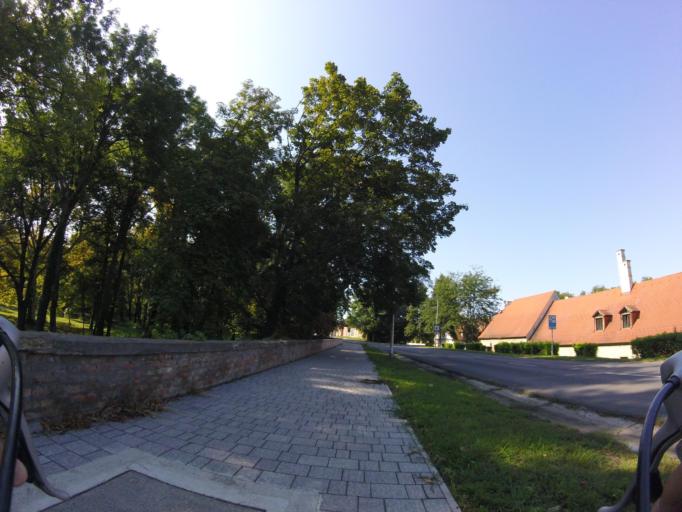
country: HU
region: Veszprem
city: Papa
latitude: 47.3353
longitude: 17.4636
